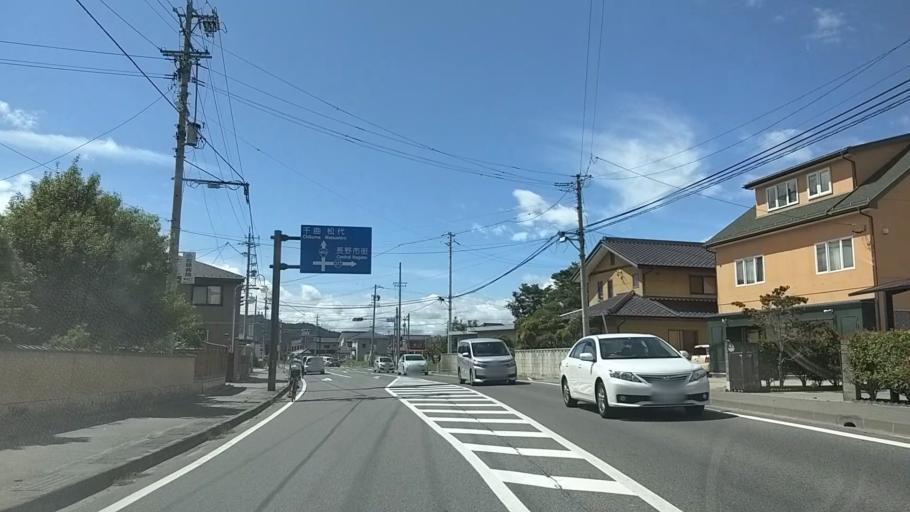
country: JP
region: Nagano
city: Suzaka
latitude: 36.6197
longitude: 138.2541
